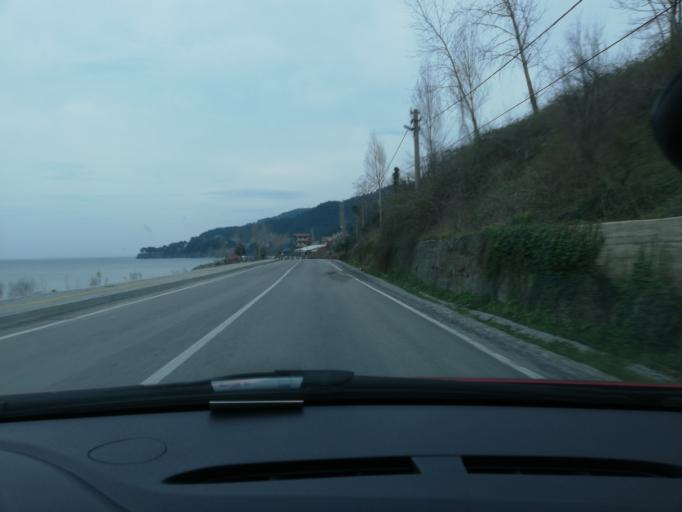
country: TR
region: Kastamonu
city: Inebolu
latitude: 41.9729
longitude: 33.7813
